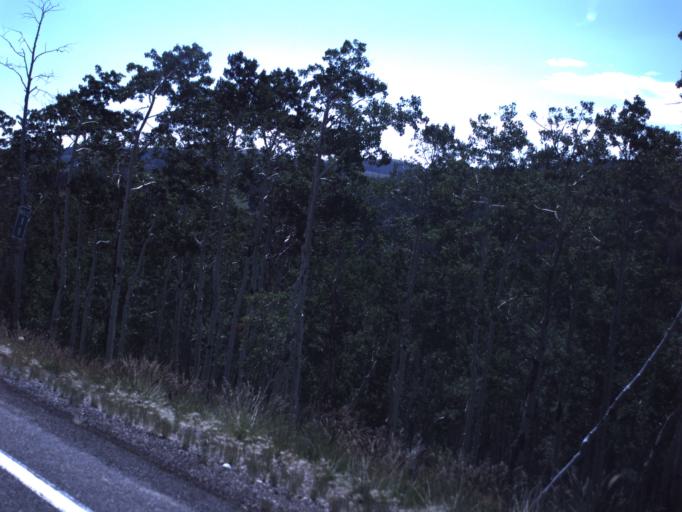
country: US
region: Utah
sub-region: Sanpete County
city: Fairview
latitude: 39.6798
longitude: -111.2187
